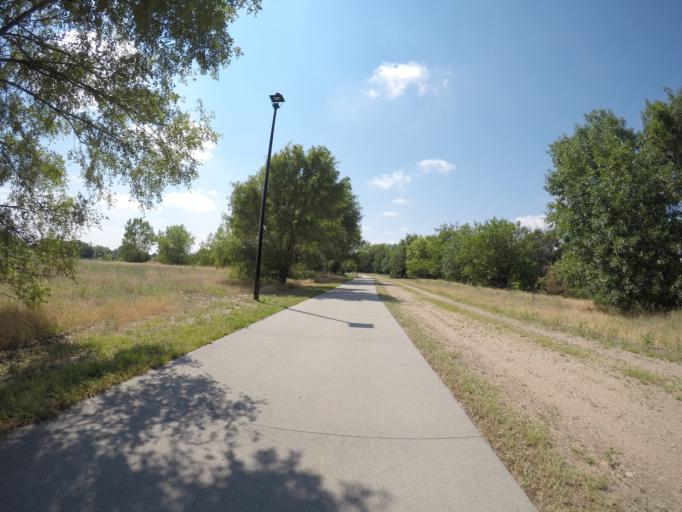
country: US
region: Nebraska
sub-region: Buffalo County
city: Kearney
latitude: 40.6726
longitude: -99.0439
